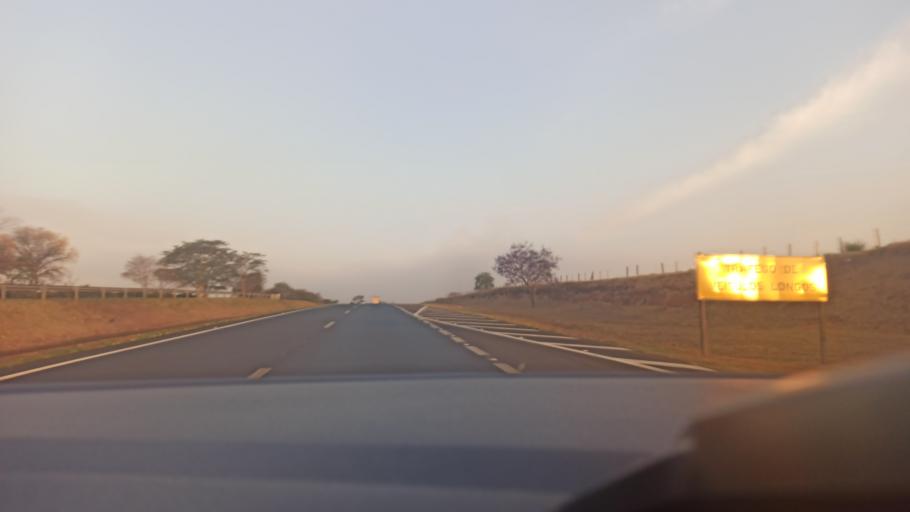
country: BR
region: Sao Paulo
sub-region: Taquaritinga
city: Taquaritinga
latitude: -21.4383
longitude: -48.6527
